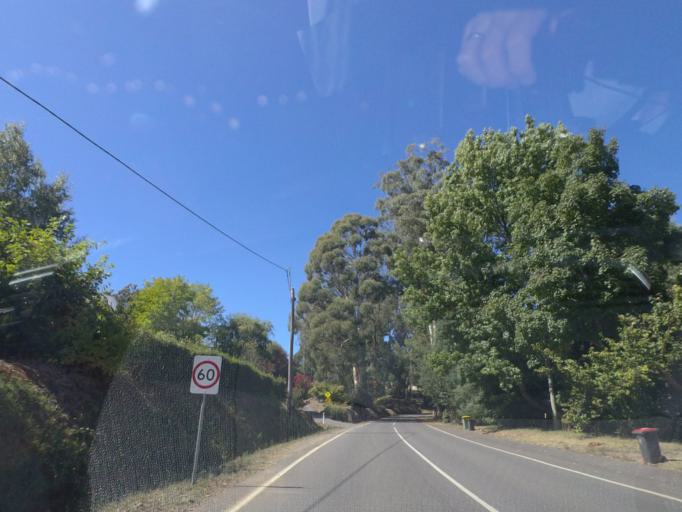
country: AU
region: Victoria
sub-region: Yarra Ranges
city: Millgrove
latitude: -37.5093
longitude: 145.7500
